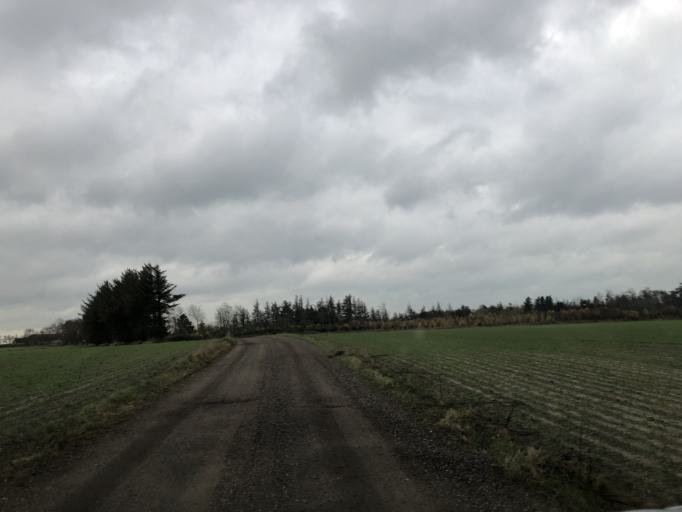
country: DK
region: Central Jutland
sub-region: Holstebro Kommune
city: Ulfborg
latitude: 56.3068
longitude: 8.2008
